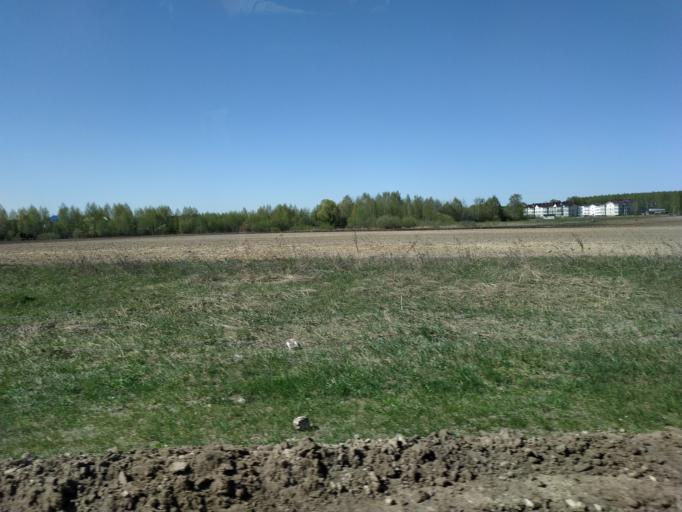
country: RU
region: Moskovskaya
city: Malyshevo
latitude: 55.4632
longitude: 38.3824
